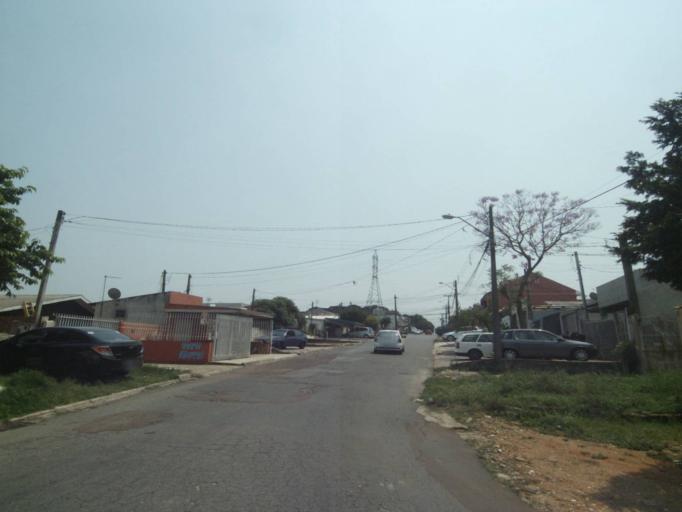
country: BR
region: Parana
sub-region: Sao Jose Dos Pinhais
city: Sao Jose dos Pinhais
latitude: -25.5278
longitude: -49.2371
